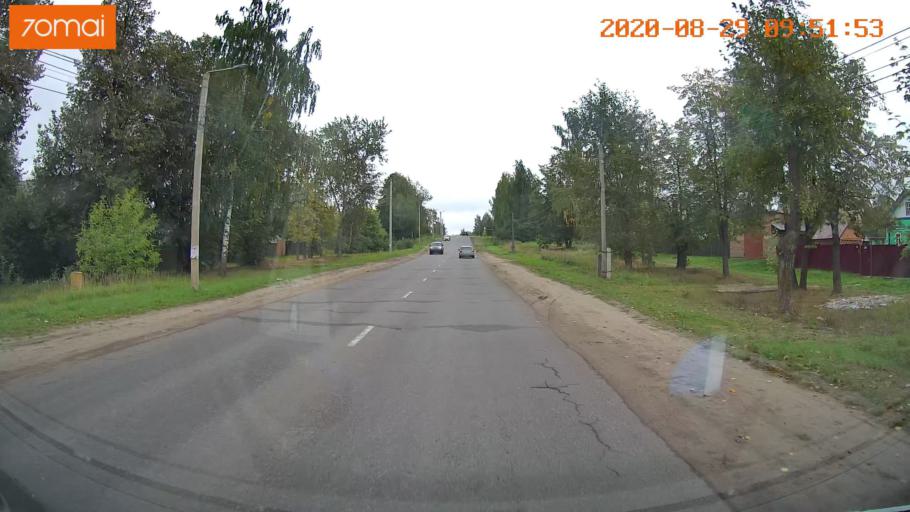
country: RU
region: Ivanovo
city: Kineshma
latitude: 57.4270
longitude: 42.2028
